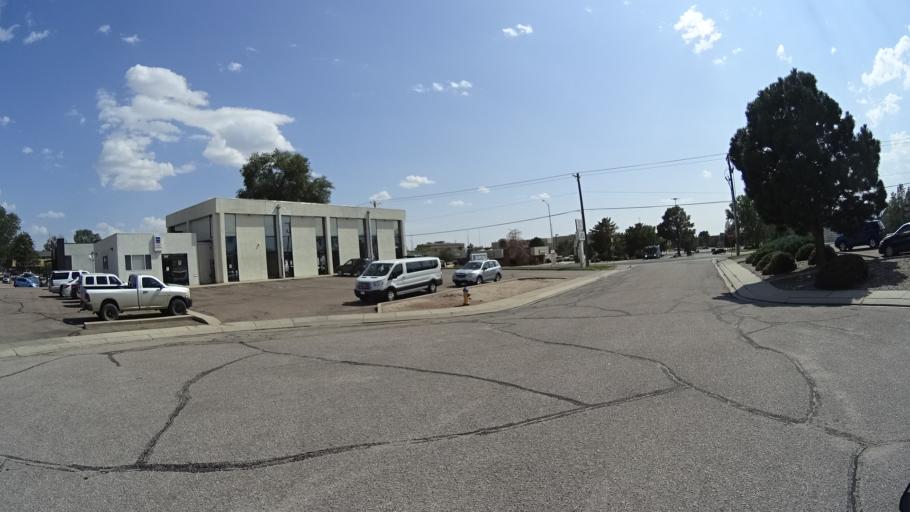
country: US
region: Colorado
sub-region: El Paso County
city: Colorado Springs
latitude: 38.8477
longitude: -104.7625
